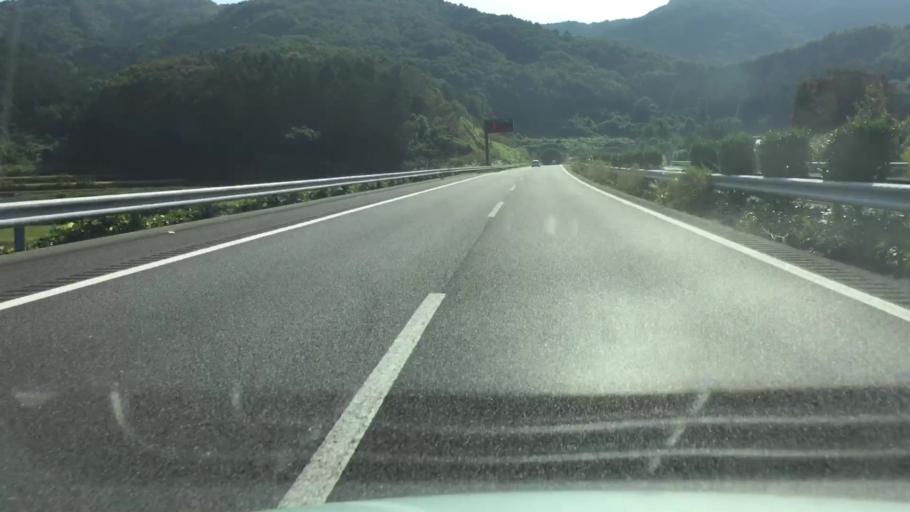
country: JP
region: Ibaraki
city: Iwase
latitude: 36.3506
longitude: 140.1040
